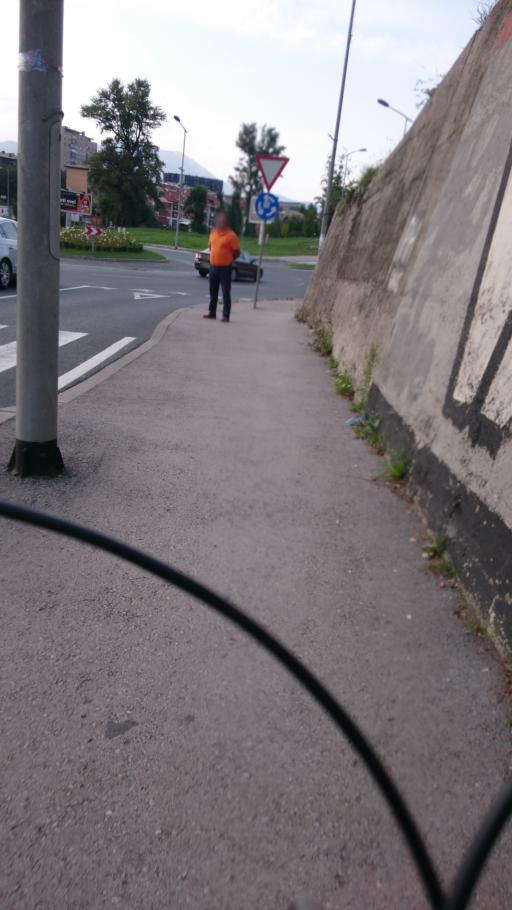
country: BA
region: Federation of Bosnia and Herzegovina
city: Zenica
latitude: 44.1966
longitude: 17.9243
